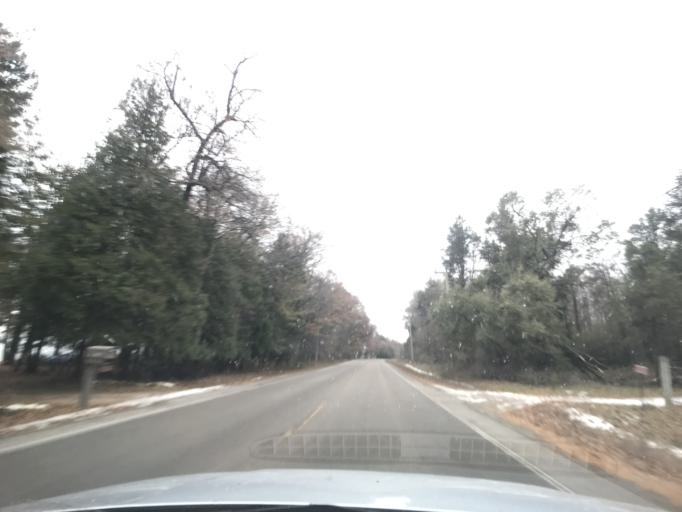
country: US
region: Wisconsin
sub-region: Marinette County
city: Marinette
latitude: 45.0594
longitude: -87.6204
